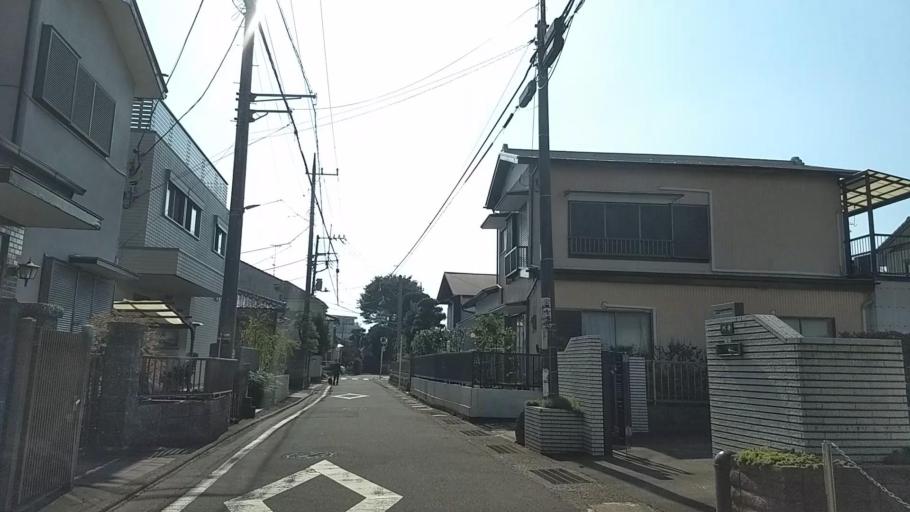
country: JP
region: Kanagawa
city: Atsugi
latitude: 35.4566
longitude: 139.3621
